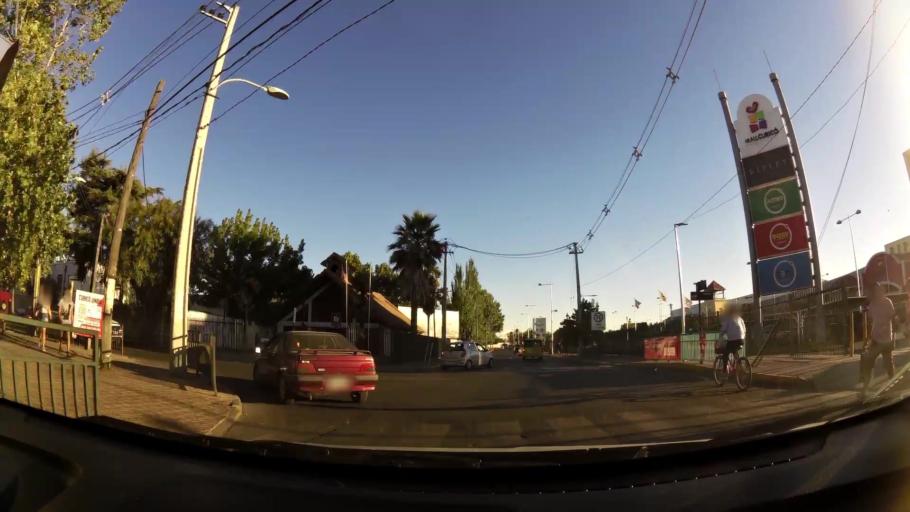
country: CL
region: Maule
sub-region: Provincia de Curico
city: Curico
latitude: -34.9897
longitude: -71.2438
